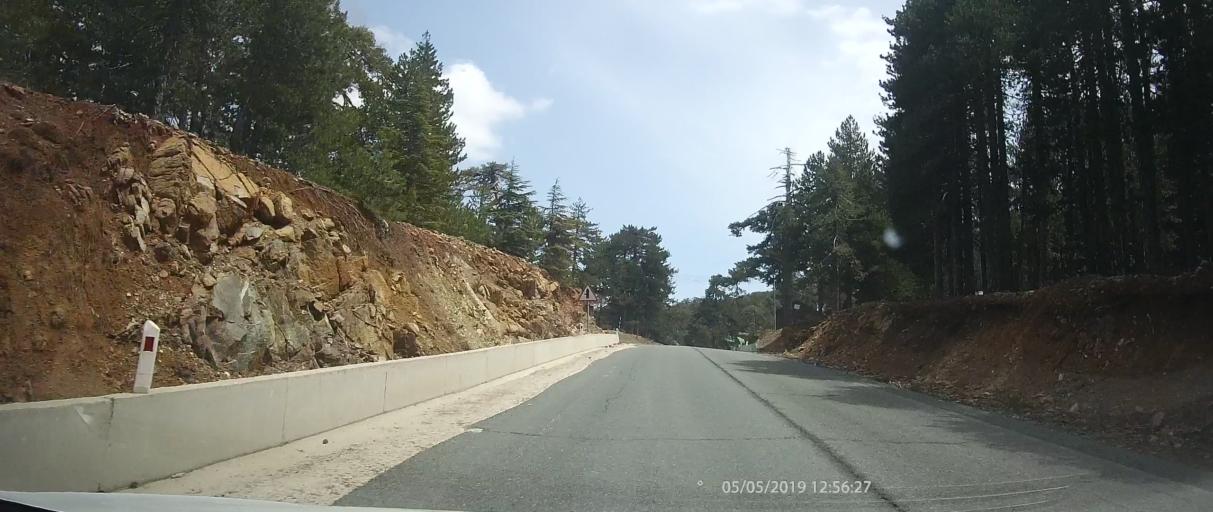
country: CY
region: Lefkosia
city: Kakopetria
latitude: 34.9415
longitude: 32.8638
